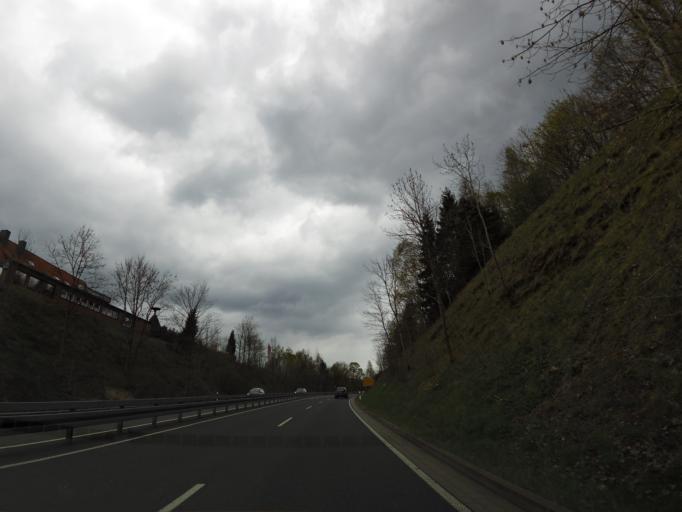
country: DE
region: Lower Saxony
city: Osterode am Harz
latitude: 51.7435
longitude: 10.2805
